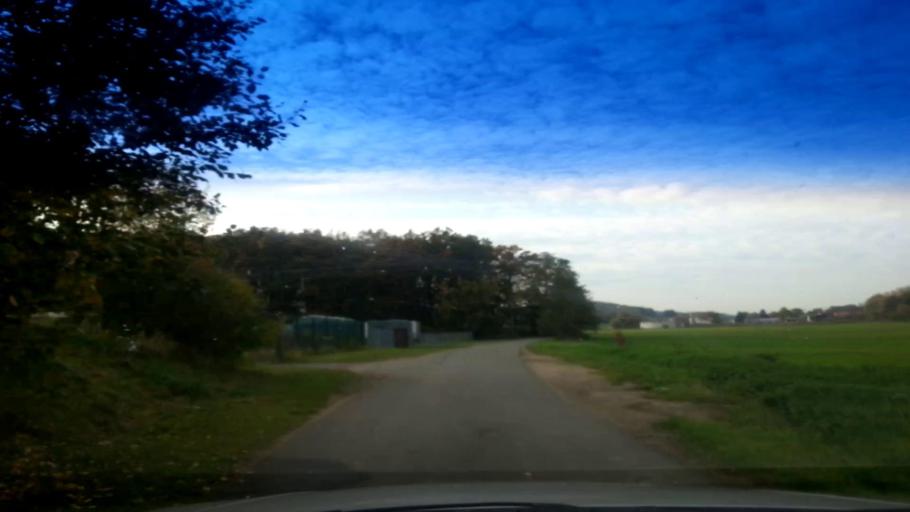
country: DE
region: Bavaria
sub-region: Upper Franconia
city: Frensdorf
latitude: 49.8500
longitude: 10.8743
